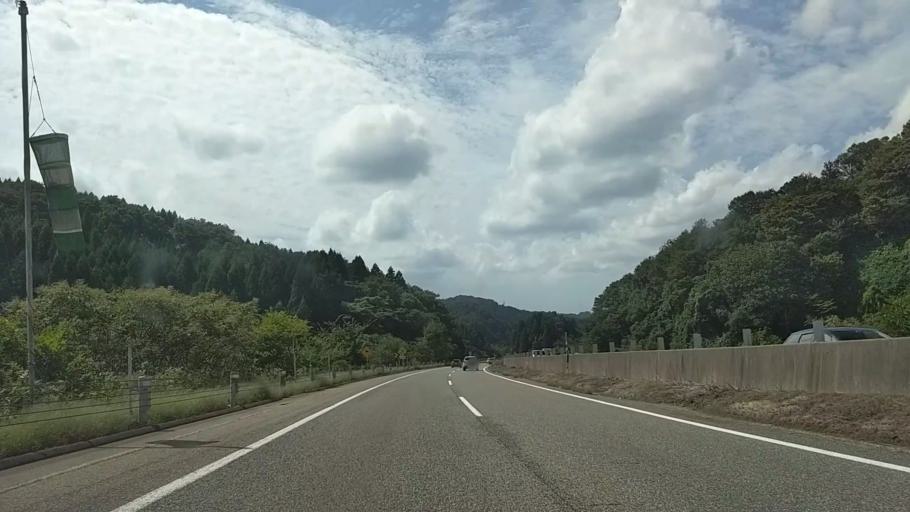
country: JP
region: Ishikawa
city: Tsubata
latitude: 36.6012
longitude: 136.7844
